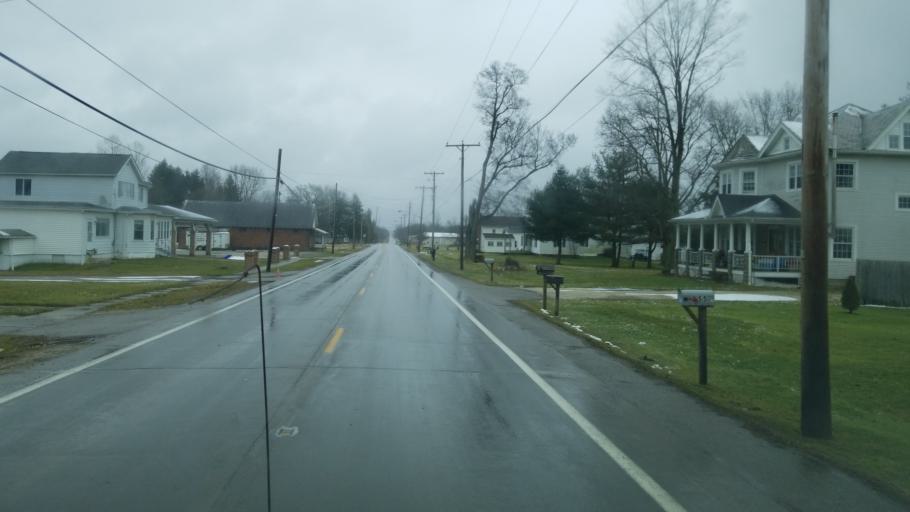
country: US
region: Ohio
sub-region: Geauga County
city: Middlefield
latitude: 41.3905
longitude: -80.9701
